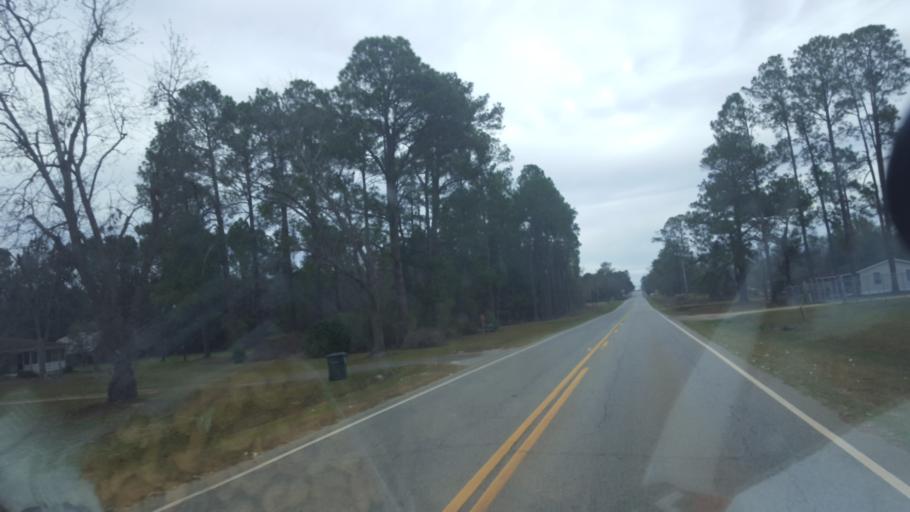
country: US
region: Georgia
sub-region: Wilcox County
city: Rochelle
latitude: 31.8000
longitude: -83.4935
